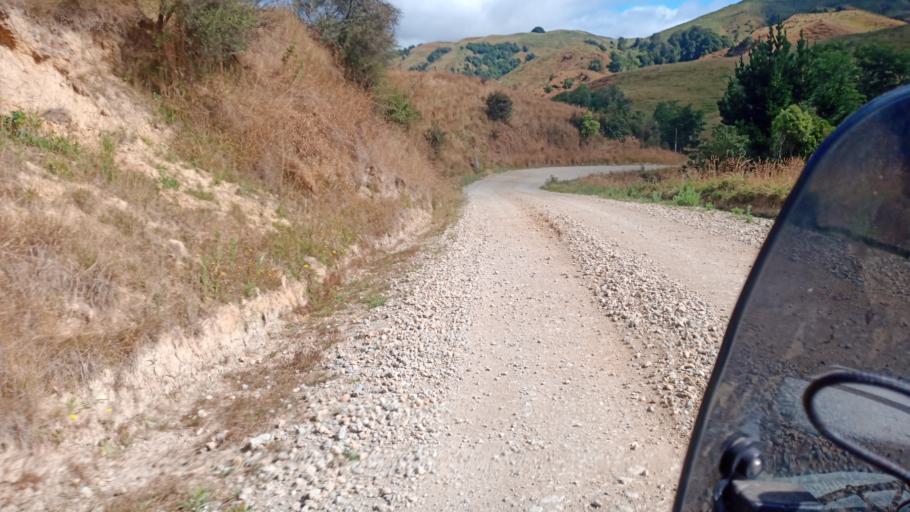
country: NZ
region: Hawke's Bay
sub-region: Wairoa District
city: Wairoa
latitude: -38.6086
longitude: 177.4606
